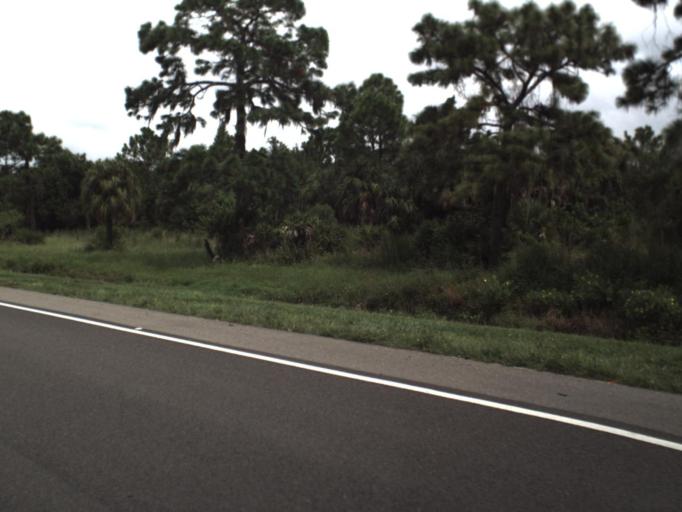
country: US
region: Florida
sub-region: Sarasota County
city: The Meadows
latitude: 27.3944
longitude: -82.4502
